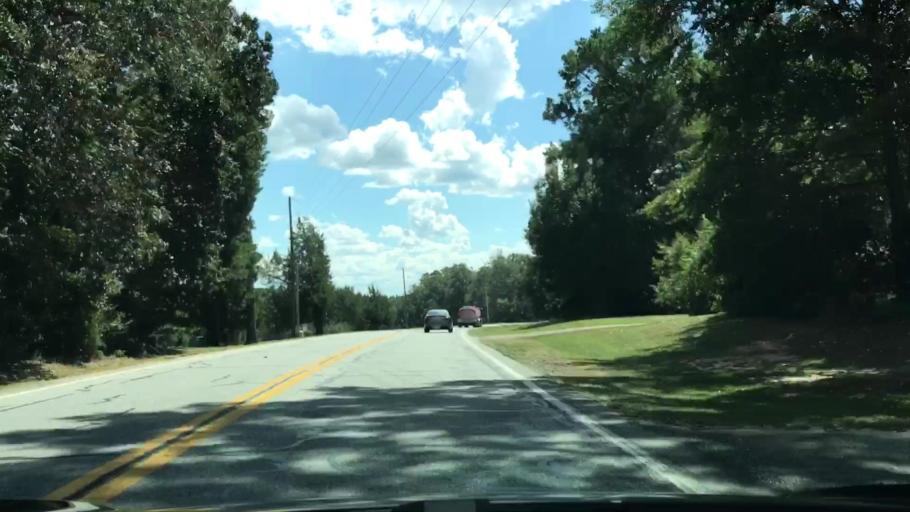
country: US
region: Georgia
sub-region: Oconee County
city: Watkinsville
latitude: 33.7485
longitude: -83.3011
